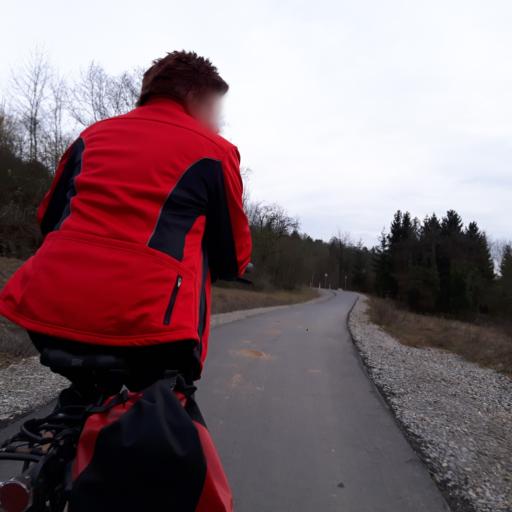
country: DE
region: Baden-Wuerttemberg
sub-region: Regierungsbezirk Stuttgart
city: Benningen am Neckar
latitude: 48.9510
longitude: 9.2526
